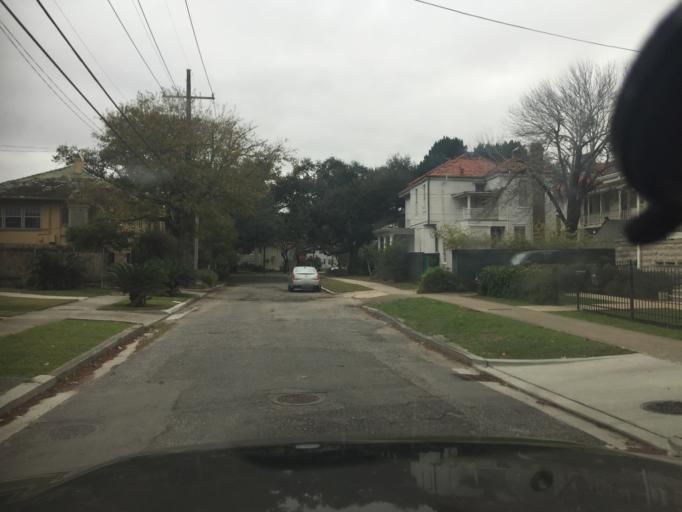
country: US
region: Louisiana
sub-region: Orleans Parish
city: New Orleans
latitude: 29.9783
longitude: -90.0852
